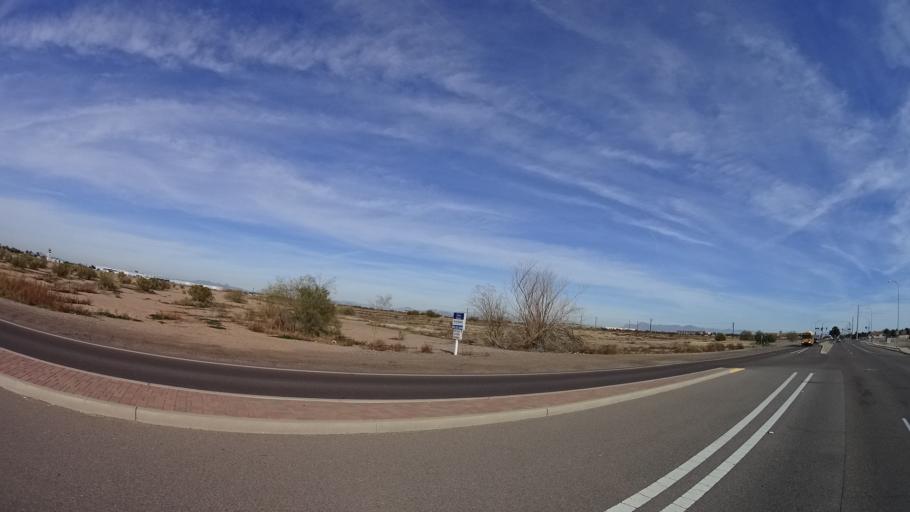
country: US
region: Arizona
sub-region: Maricopa County
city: Chandler
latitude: 33.2625
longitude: -111.8096
